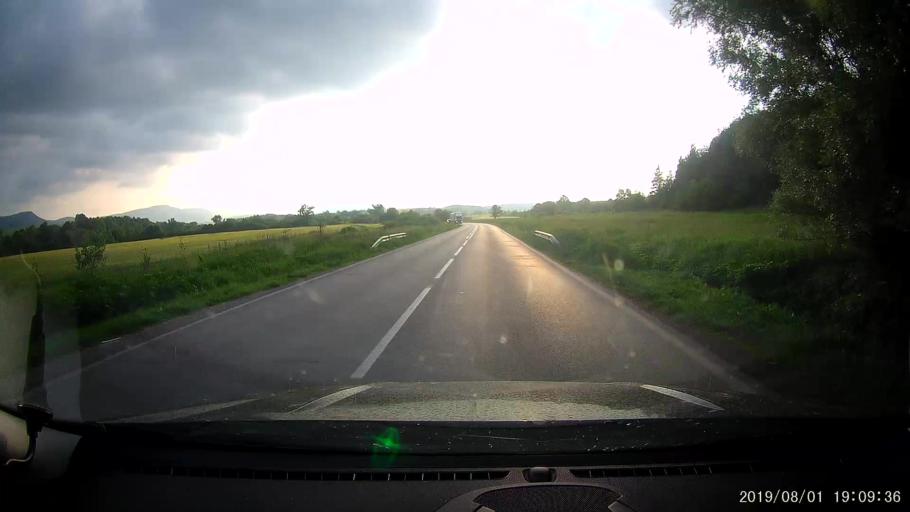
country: BG
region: Shumen
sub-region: Obshtina Smyadovo
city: Smyadovo
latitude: 42.9849
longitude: 26.9997
